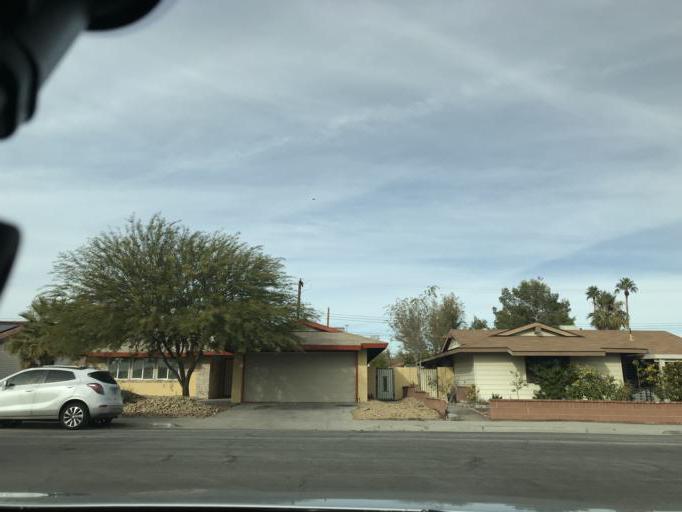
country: US
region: Nevada
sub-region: Clark County
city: Las Vegas
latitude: 36.1733
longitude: -115.1682
